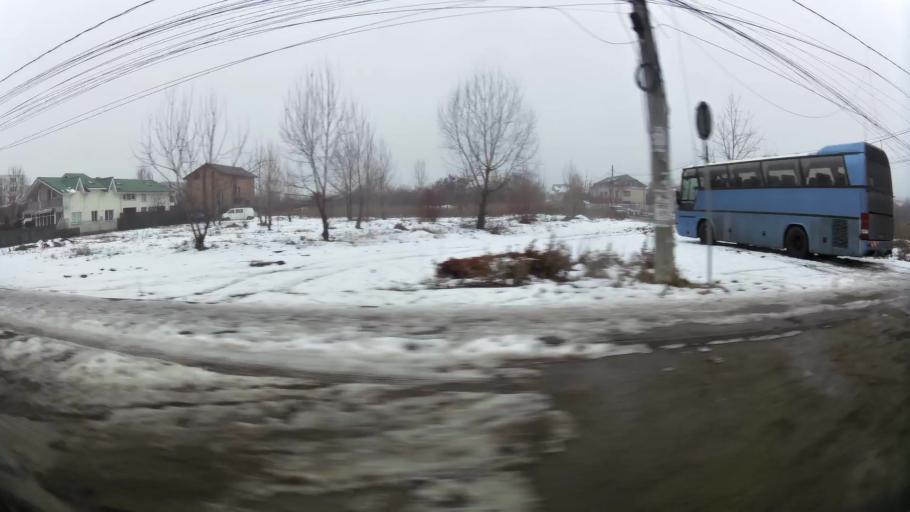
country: RO
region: Ilfov
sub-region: Comuna Bragadiru
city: Bragadiru
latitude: 44.4093
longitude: 25.9959
